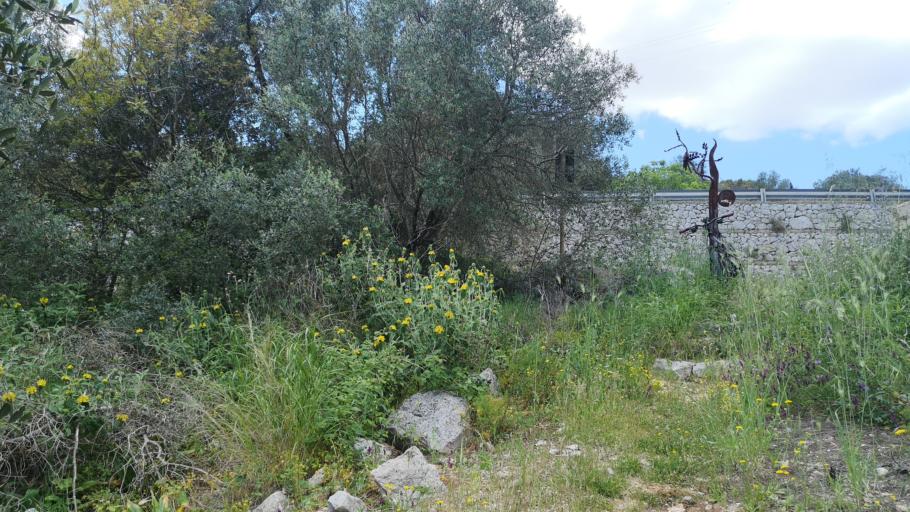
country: IT
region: Apulia
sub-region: Provincia di Lecce
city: Marittima
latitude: 39.9882
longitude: 18.4101
